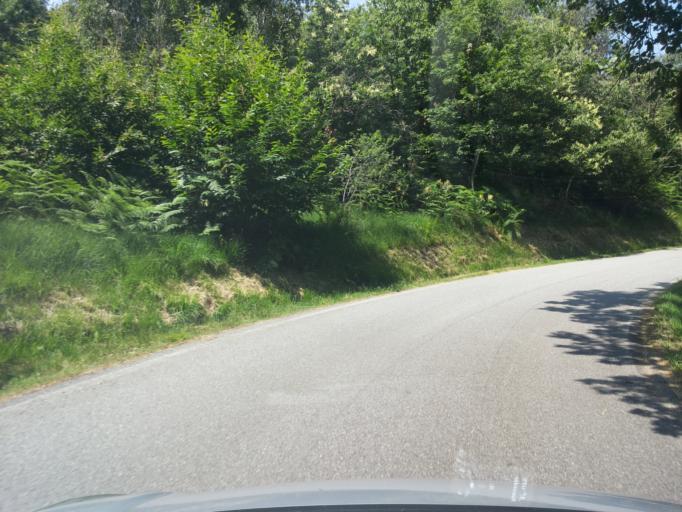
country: IT
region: Piedmont
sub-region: Provincia di Biella
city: Soprana
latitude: 45.6531
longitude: 8.2114
